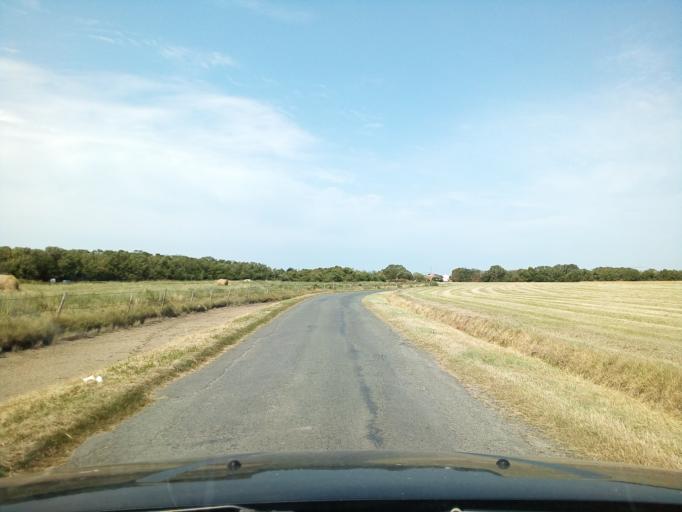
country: FR
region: Poitou-Charentes
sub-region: Departement de la Charente-Maritime
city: Dolus-d'Oleron
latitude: 45.9474
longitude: -1.2910
